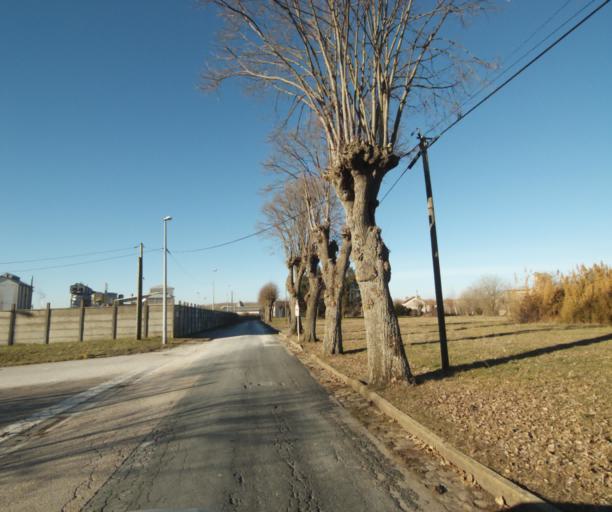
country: FR
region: Lorraine
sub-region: Departement de Meurthe-et-Moselle
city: Art-sur-Meurthe
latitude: 48.6377
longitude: 6.2687
